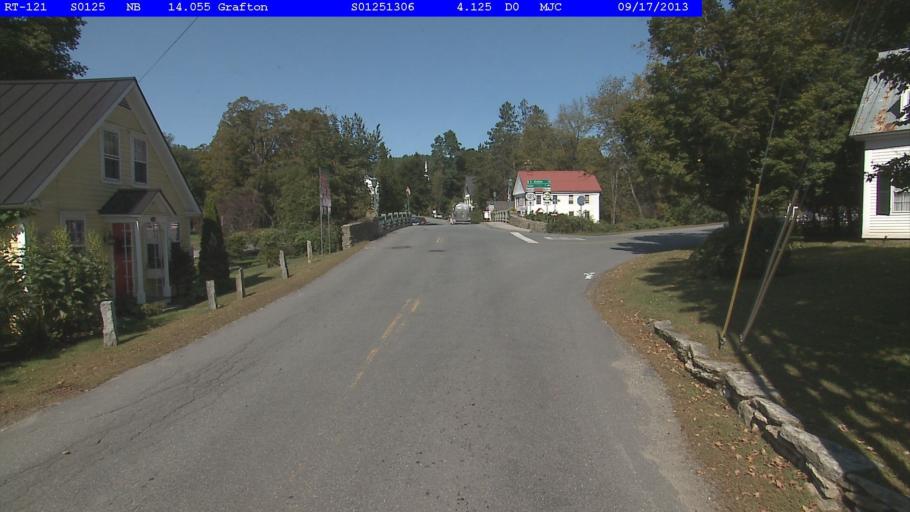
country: US
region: Vermont
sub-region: Windsor County
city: Chester
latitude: 43.1712
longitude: -72.6060
